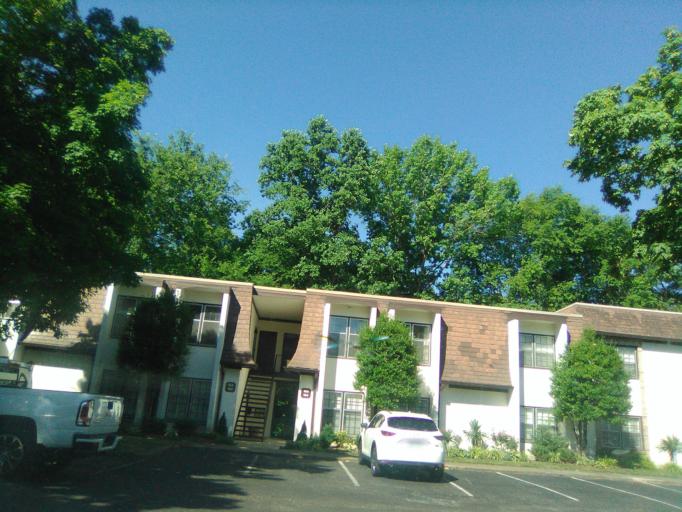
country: US
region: Tennessee
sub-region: Davidson County
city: Belle Meade
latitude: 36.1218
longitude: -86.8482
